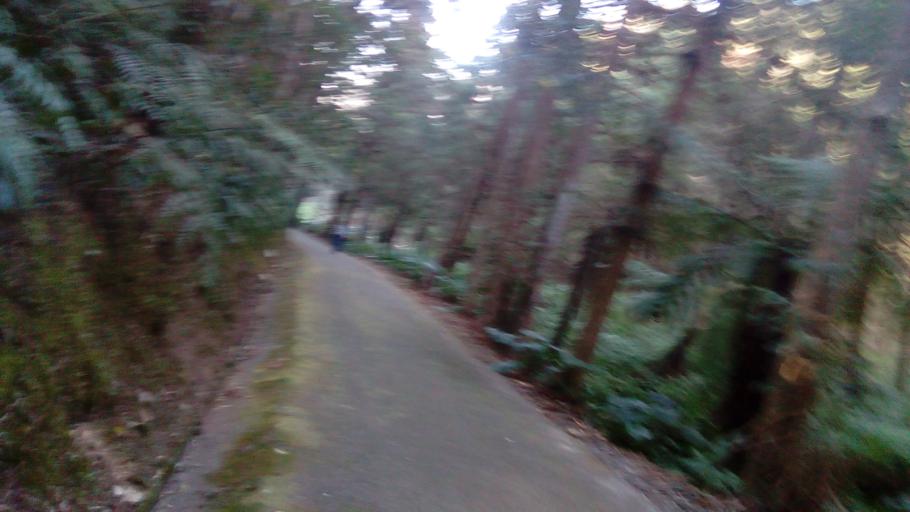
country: TW
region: Taiwan
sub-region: Nantou
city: Puli
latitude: 24.0924
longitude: 121.0333
